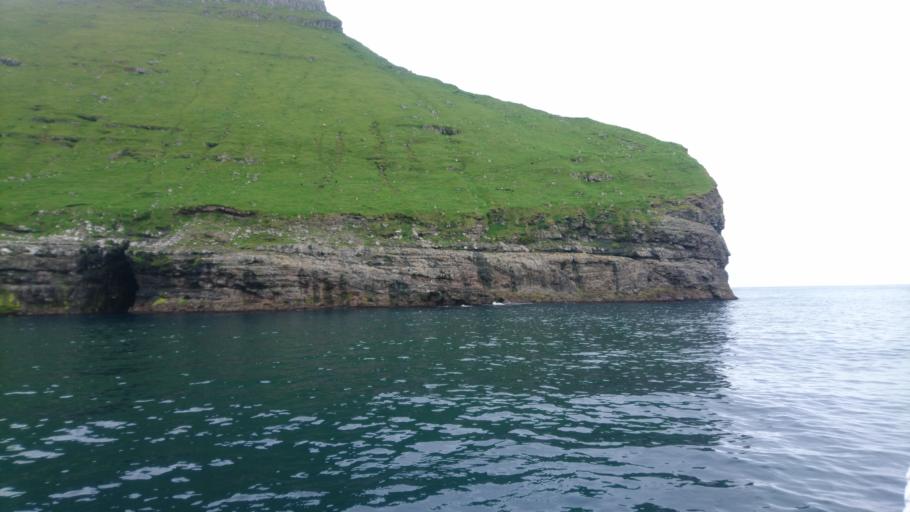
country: FO
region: Nordoyar
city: Klaksvik
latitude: 62.3262
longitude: -6.2693
